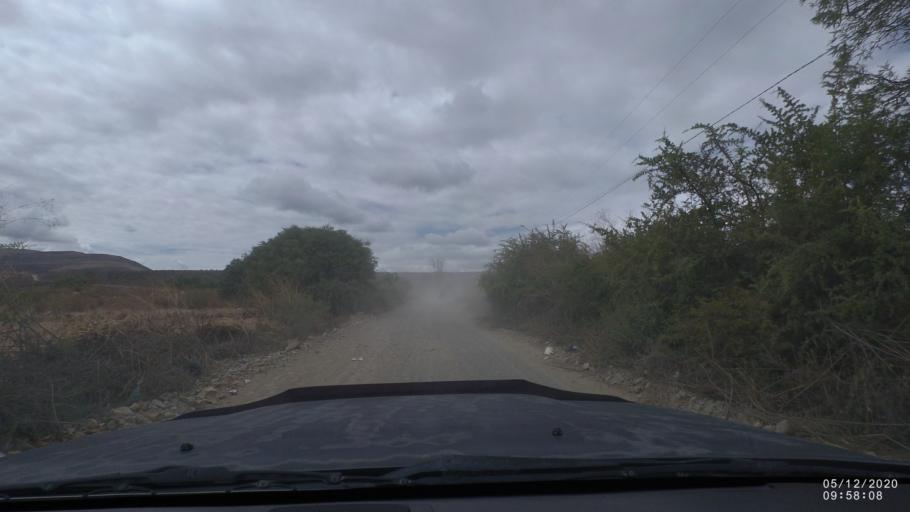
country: BO
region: Cochabamba
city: Sipe Sipe
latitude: -17.4276
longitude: -66.2909
